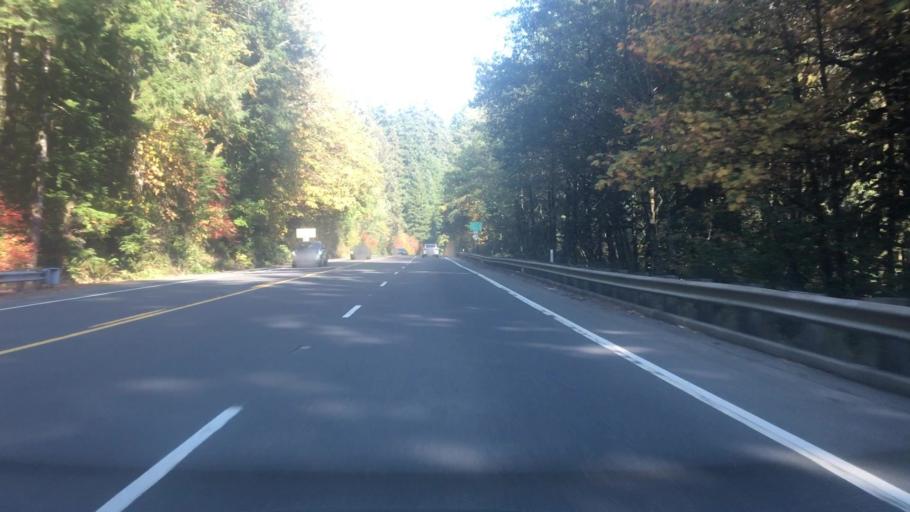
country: US
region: Oregon
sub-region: Lincoln County
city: Rose Lodge
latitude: 45.0442
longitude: -123.8023
